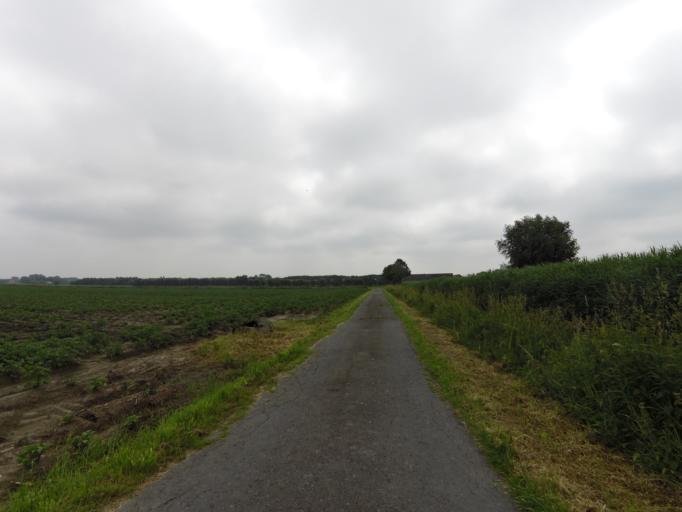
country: BE
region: Flanders
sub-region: Provincie West-Vlaanderen
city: Oudenburg
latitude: 51.1514
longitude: 3.0388
